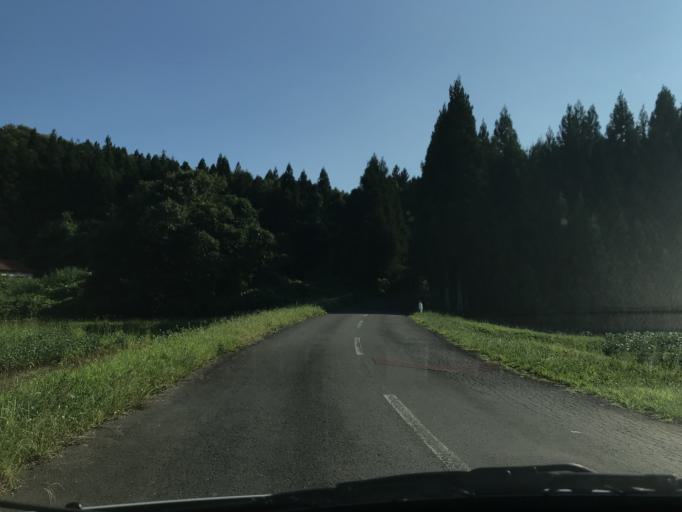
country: JP
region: Iwate
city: Mizusawa
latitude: 39.1226
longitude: 140.9986
